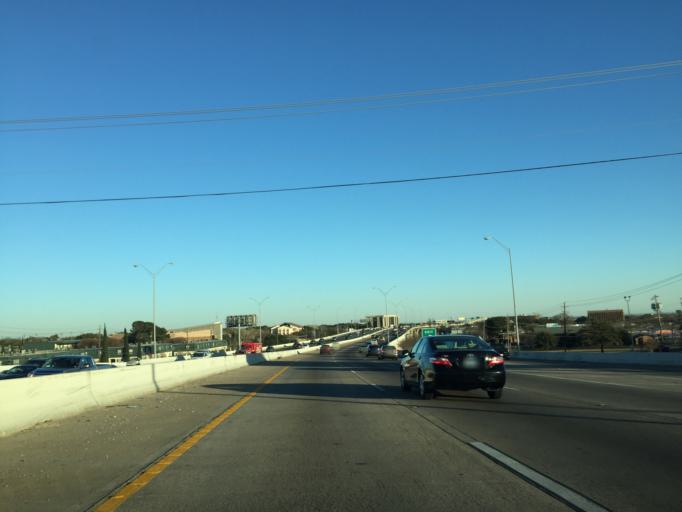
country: US
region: Texas
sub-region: Travis County
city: Austin
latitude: 30.3462
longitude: -97.7098
